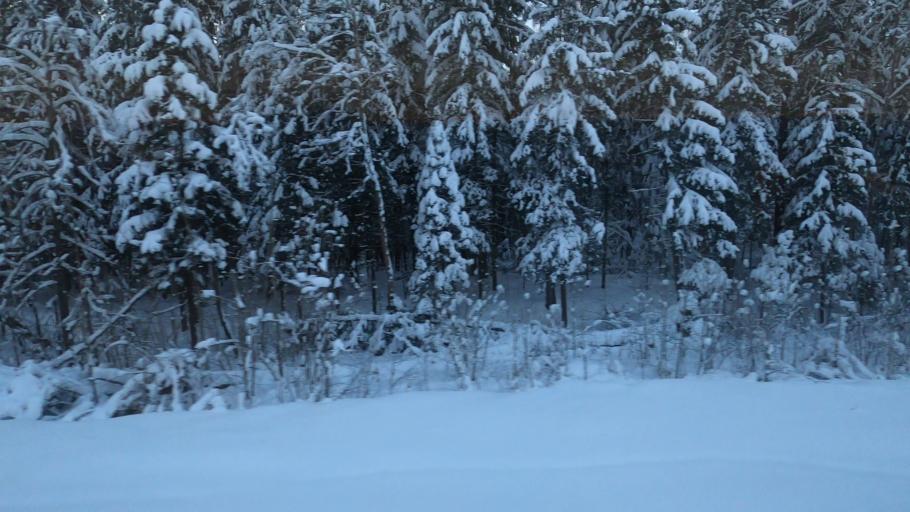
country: RU
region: Moskovskaya
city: Novo-Nikol'skoye
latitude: 56.5569
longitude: 37.5651
